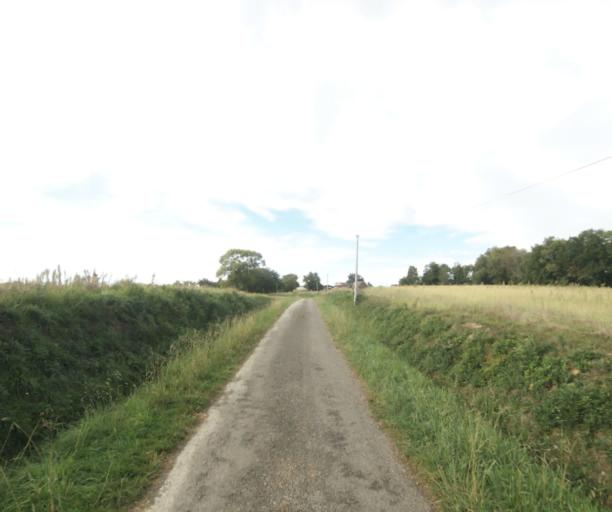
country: FR
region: Midi-Pyrenees
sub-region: Departement du Gers
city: Cazaubon
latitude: 43.8684
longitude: -0.1322
